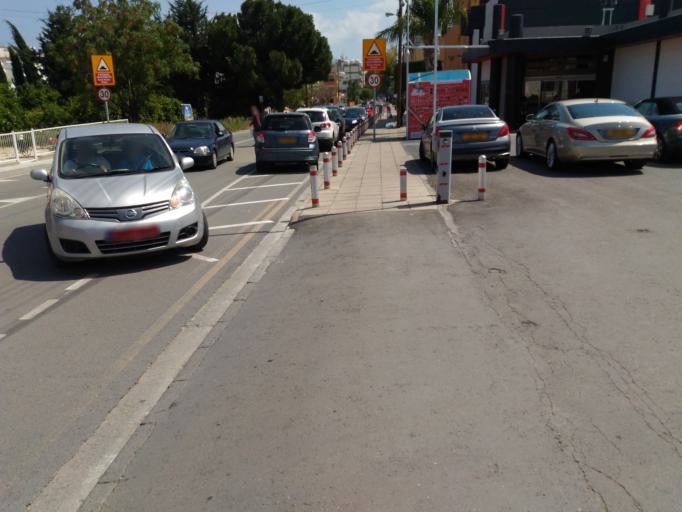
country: CY
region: Limassol
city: Mouttagiaka
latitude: 34.6958
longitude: 33.0805
